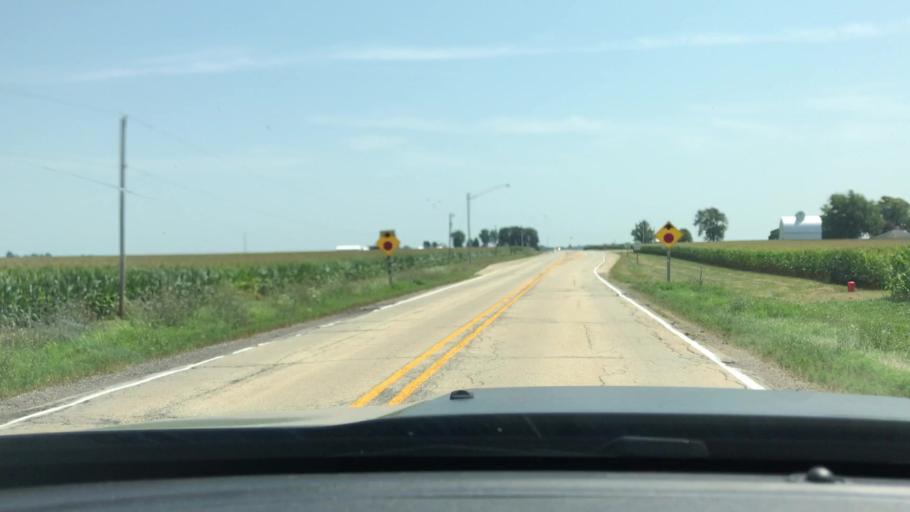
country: US
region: Illinois
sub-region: LaSalle County
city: Ottawa
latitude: 41.4704
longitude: -88.8430
